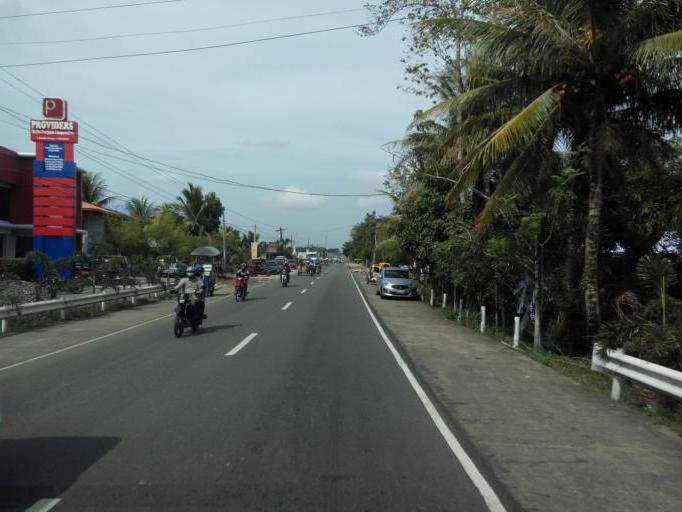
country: PH
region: Cagayan Valley
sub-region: Province of Isabela
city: Naguilian
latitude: 17.0221
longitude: 121.8538
